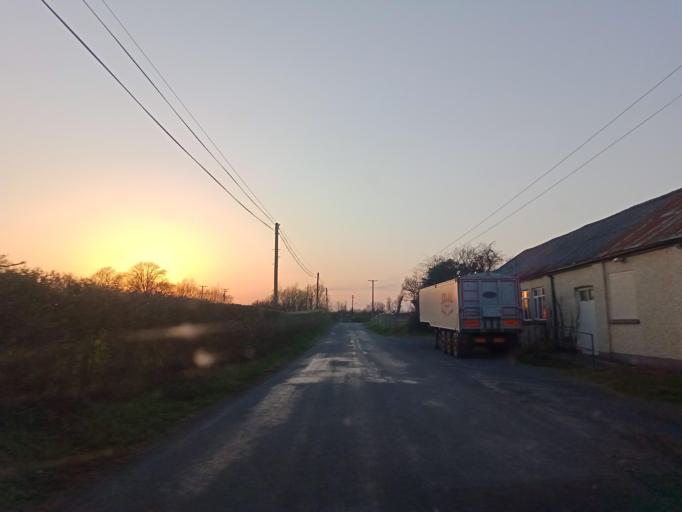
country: IE
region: Leinster
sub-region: Laois
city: Abbeyleix
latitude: 52.9530
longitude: -7.3585
